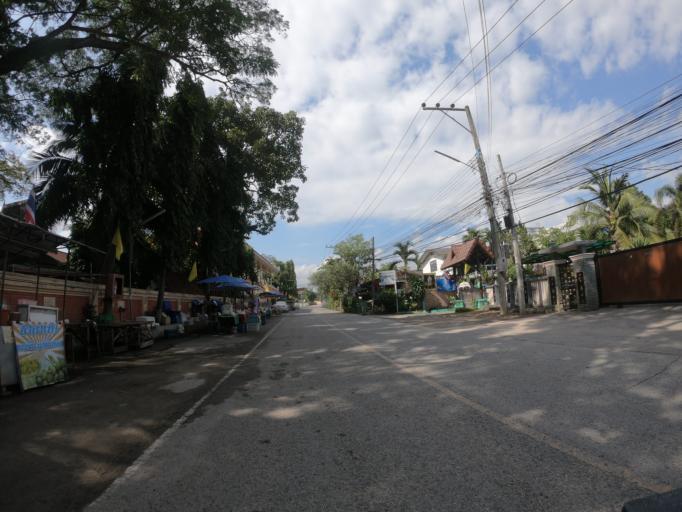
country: TH
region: Chiang Mai
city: Chiang Mai
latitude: 18.7353
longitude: 98.9579
